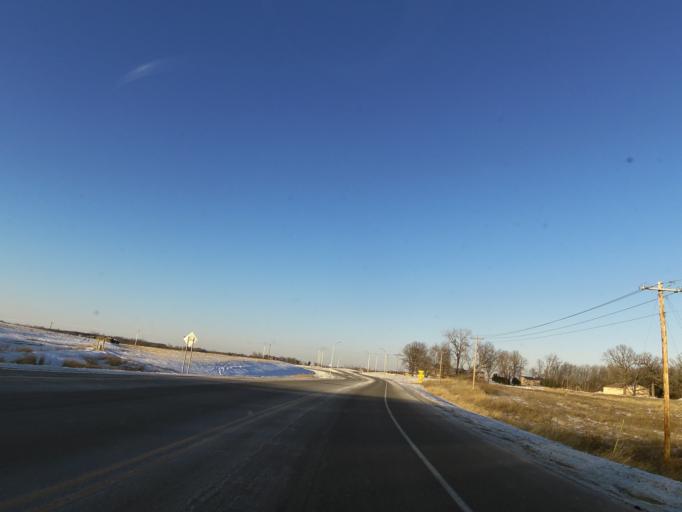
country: US
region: Minnesota
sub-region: Rice County
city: Lonsdale
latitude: 44.5410
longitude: -93.4427
